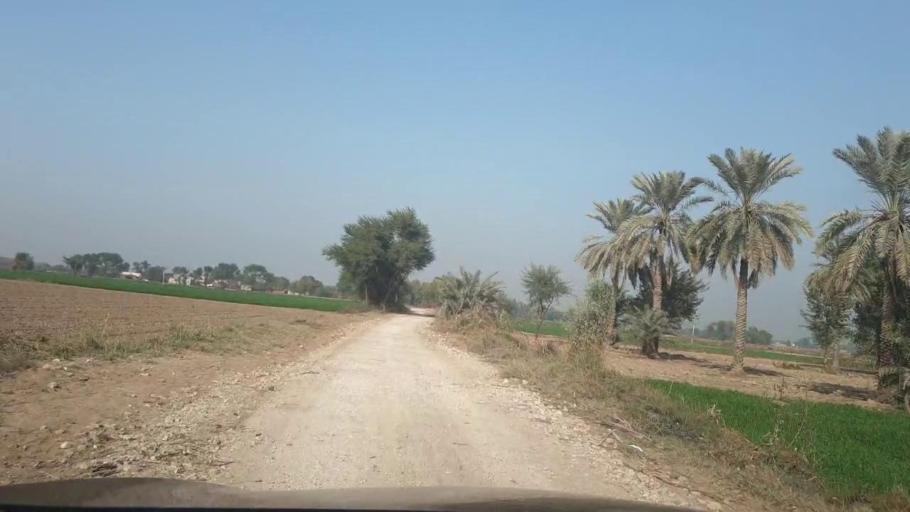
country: PK
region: Sindh
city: Ubauro
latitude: 28.0919
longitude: 69.8412
